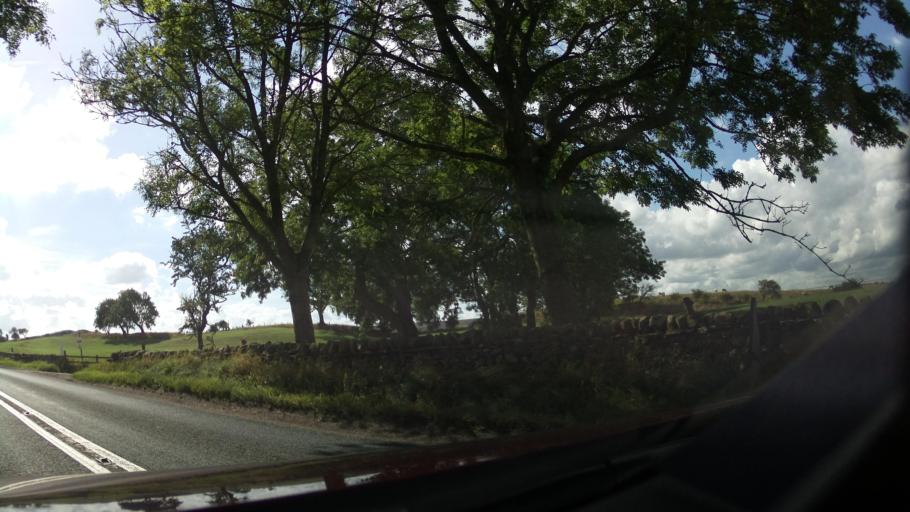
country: GB
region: England
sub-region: North Yorkshire
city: Leyburn
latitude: 54.3482
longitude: -1.8096
